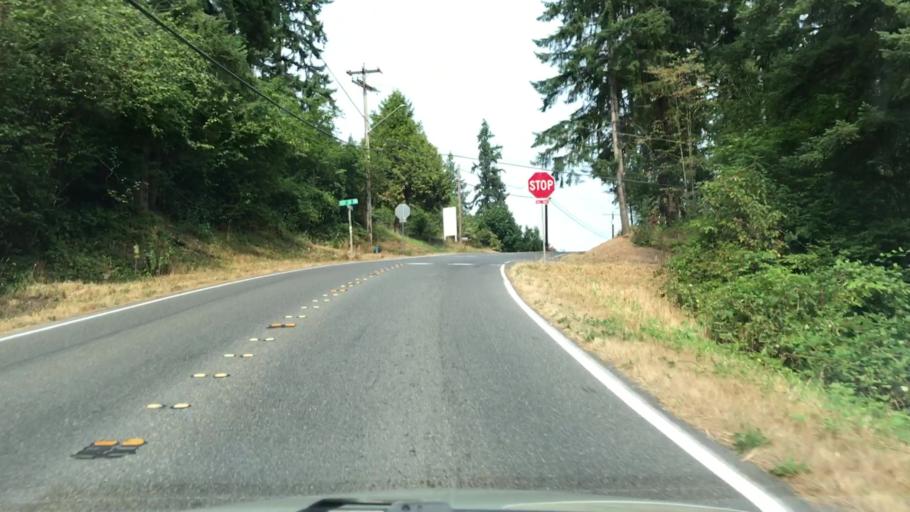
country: US
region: Washington
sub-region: Snohomish County
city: Martha Lake
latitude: 47.8737
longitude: -122.2403
